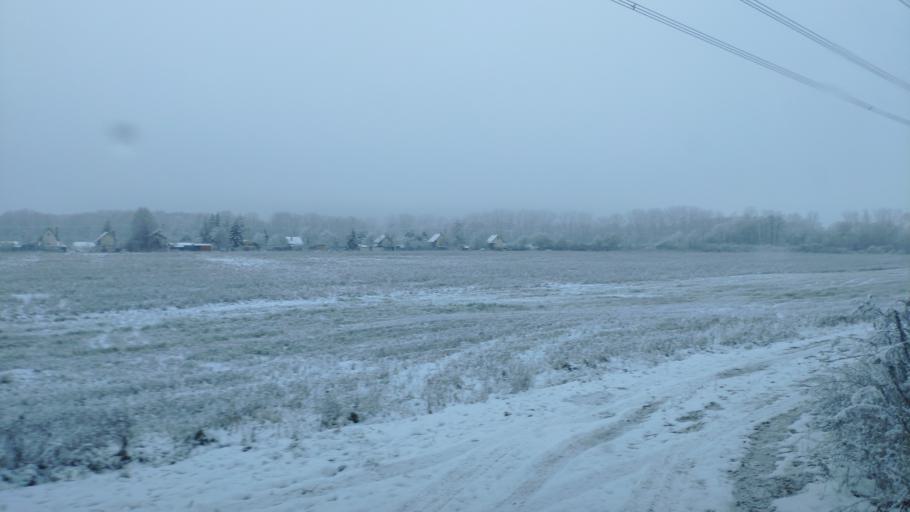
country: SK
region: Kosicky
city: Kosice
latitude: 48.6465
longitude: 21.1718
